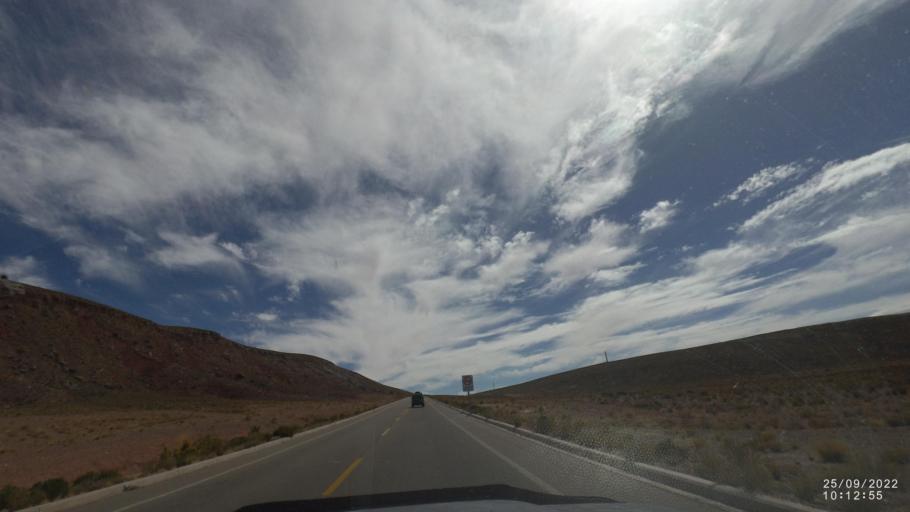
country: BO
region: Potosi
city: Colchani
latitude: -20.0800
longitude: -66.8904
